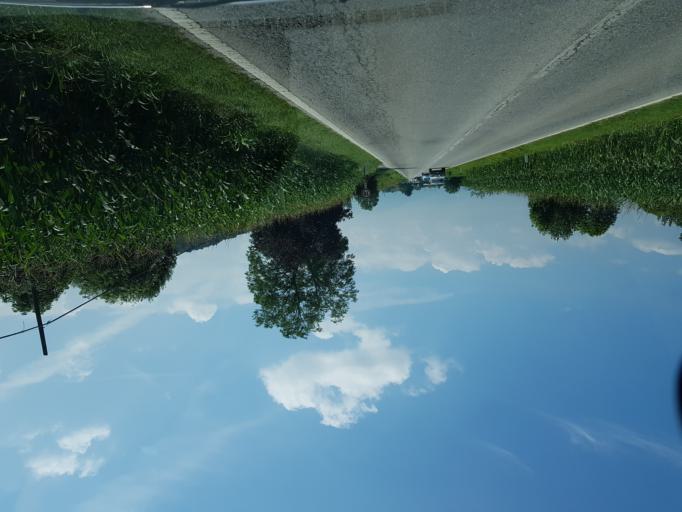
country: IT
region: Piedmont
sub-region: Provincia di Cuneo
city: Caraglio
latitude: 44.4381
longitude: 7.4147
